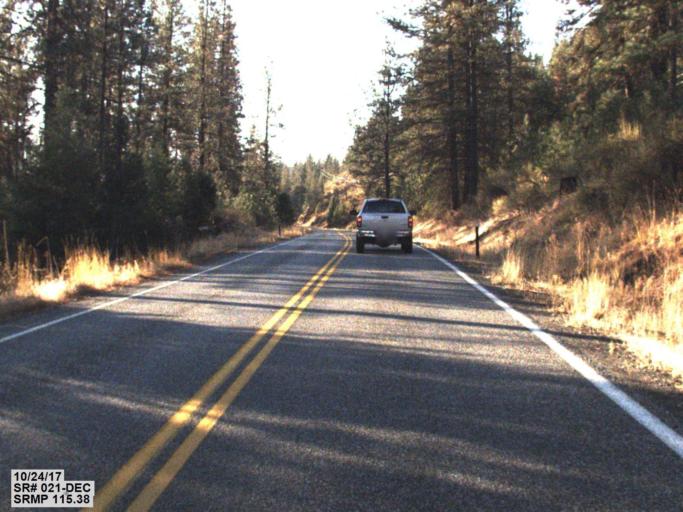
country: US
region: Washington
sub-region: Okanogan County
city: Coulee Dam
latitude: 48.0619
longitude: -118.6735
